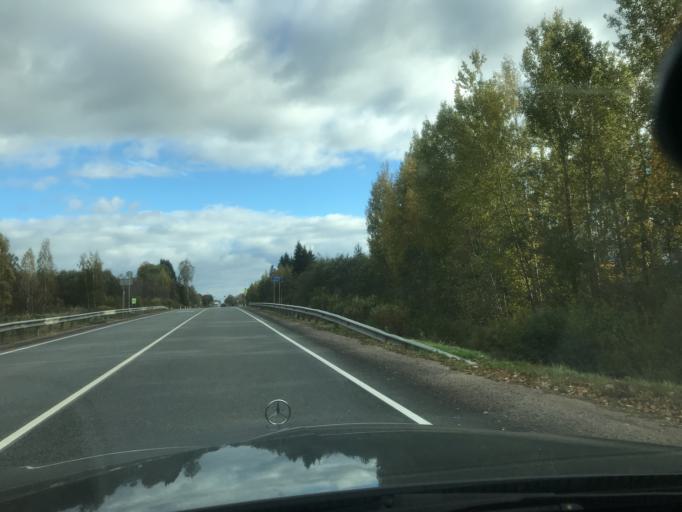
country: RU
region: Pskov
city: Opochka
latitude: 56.6746
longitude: 28.7212
